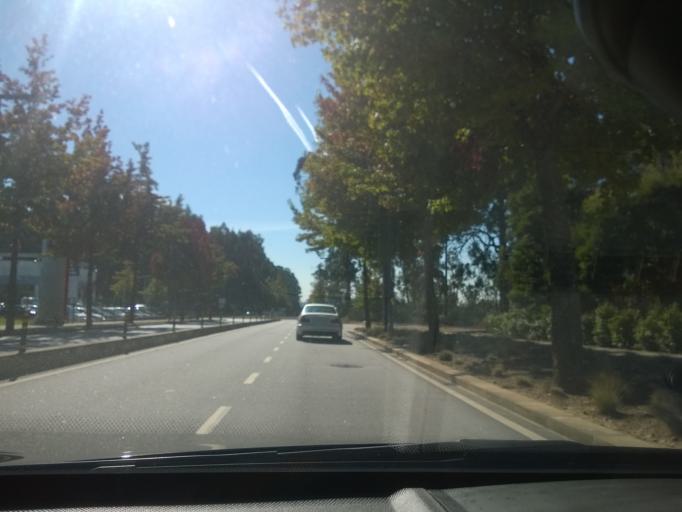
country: PT
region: Porto
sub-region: Maia
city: Anta
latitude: 41.2573
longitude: -8.6335
